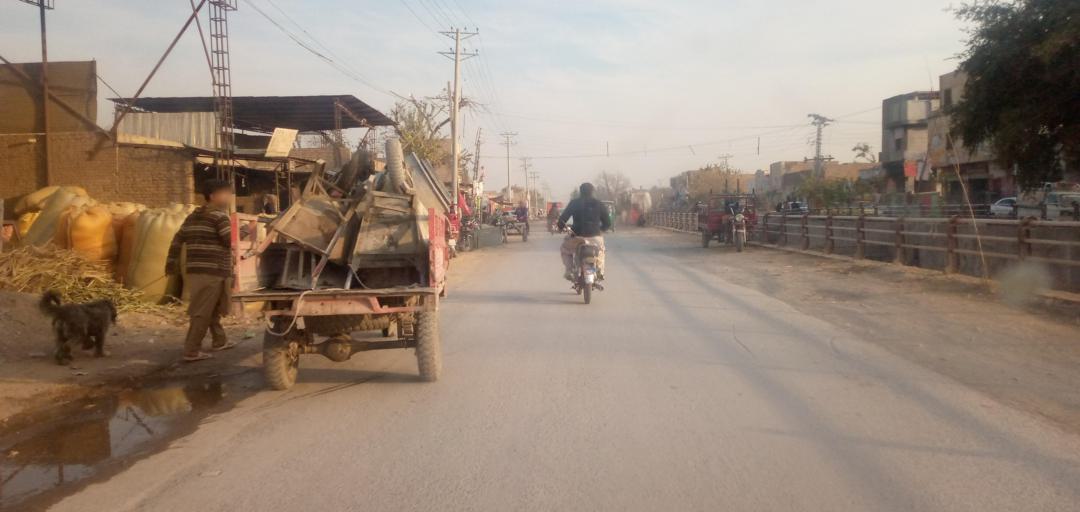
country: PK
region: Khyber Pakhtunkhwa
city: Peshawar
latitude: 33.9735
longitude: 71.5297
